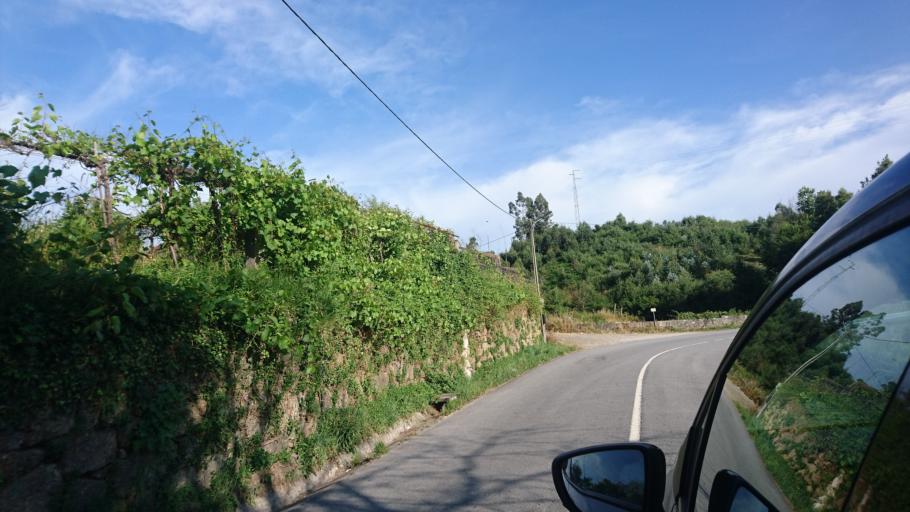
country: PT
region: Porto
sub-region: Paredes
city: Recarei
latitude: 41.1418
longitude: -8.3853
